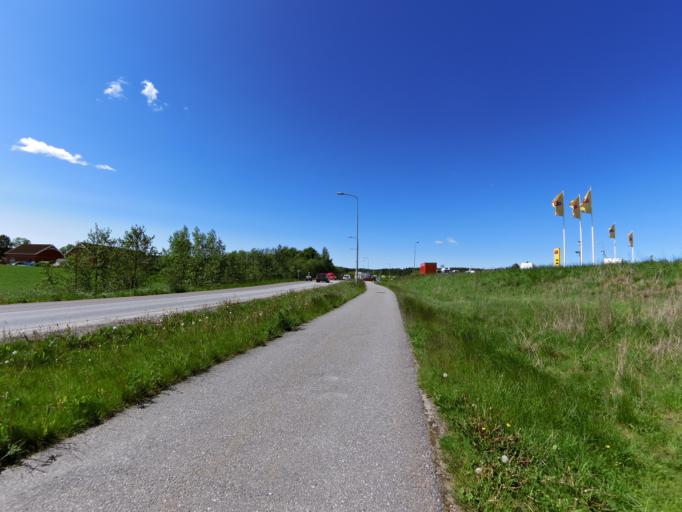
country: NO
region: Ostfold
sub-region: Fredrikstad
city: Fredrikstad
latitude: 59.2419
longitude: 10.9830
